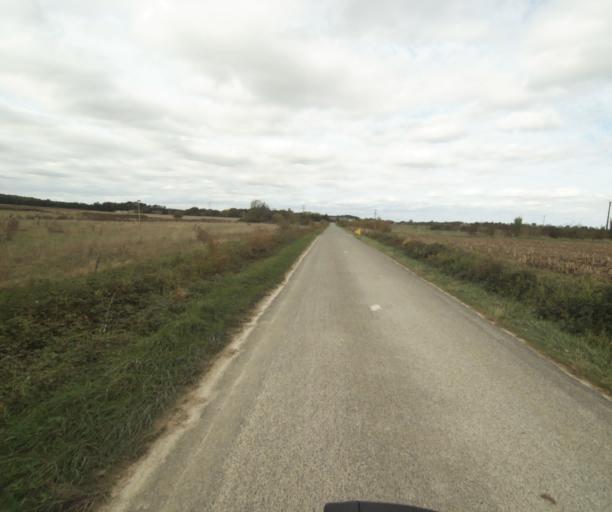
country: FR
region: Midi-Pyrenees
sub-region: Departement du Tarn-et-Garonne
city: Finhan
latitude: 43.8710
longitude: 1.1495
